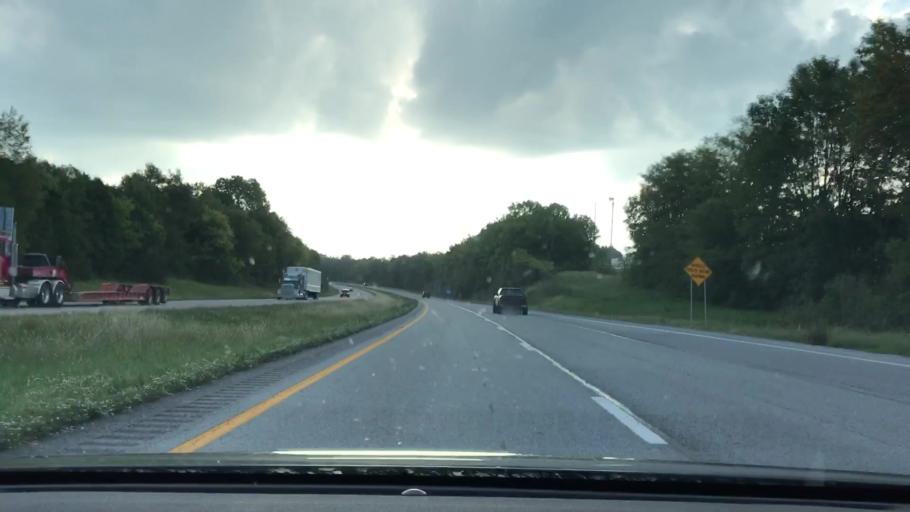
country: US
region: Kentucky
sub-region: Barren County
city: Glasgow
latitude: 36.9756
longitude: -85.9301
